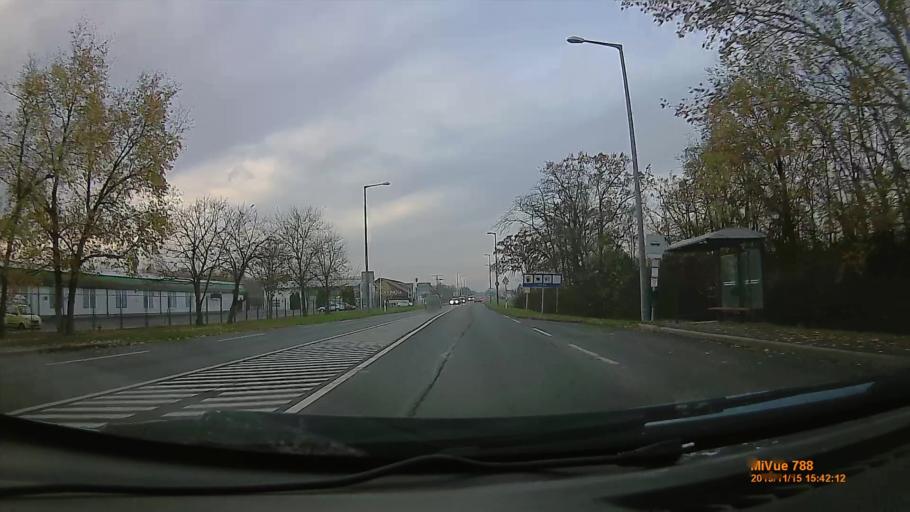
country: HU
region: Bekes
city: Bekescsaba
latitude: 46.6770
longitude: 21.1280
